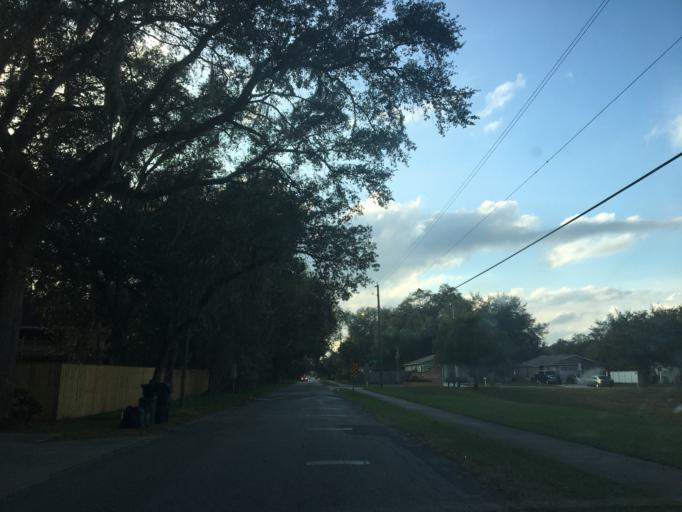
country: US
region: Florida
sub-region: Hillsborough County
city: Temple Terrace
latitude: 28.0253
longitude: -82.4058
